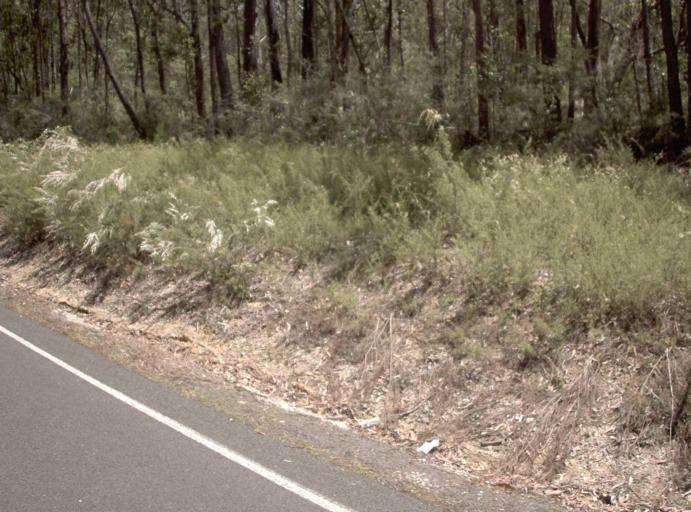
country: AU
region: Victoria
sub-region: East Gippsland
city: Lakes Entrance
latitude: -37.5945
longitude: 147.8924
